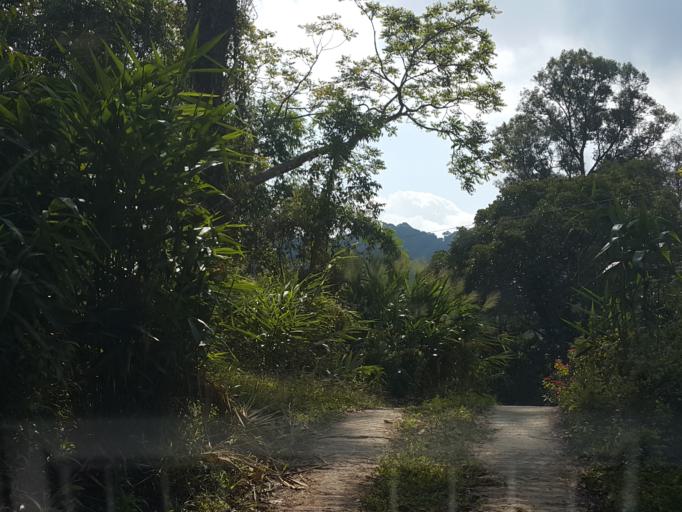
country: TH
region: Chiang Mai
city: Mae On
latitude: 18.9026
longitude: 99.3564
